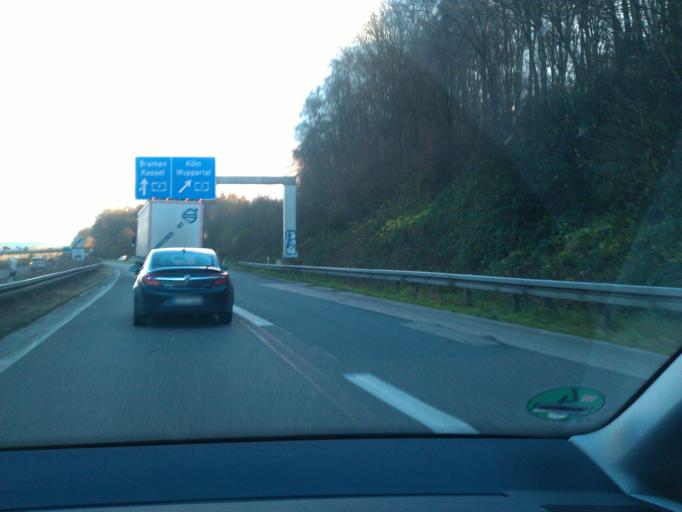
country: DE
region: North Rhine-Westphalia
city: Schwerte
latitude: 51.4348
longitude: 7.5258
